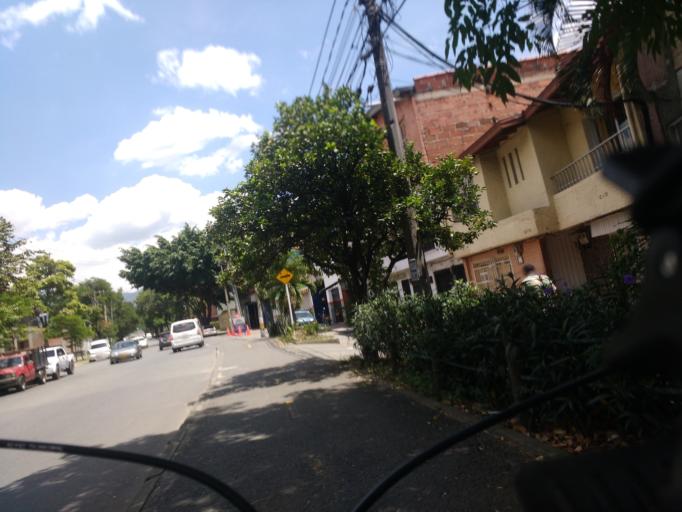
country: CO
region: Antioquia
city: Medellin
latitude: 6.2333
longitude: -75.5840
